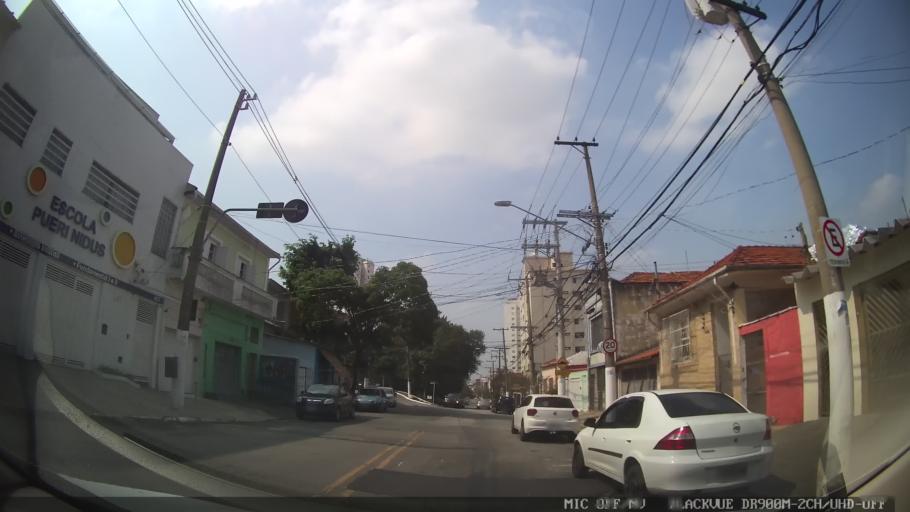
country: BR
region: Sao Paulo
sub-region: Sao Paulo
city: Sao Paulo
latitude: -23.5797
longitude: -46.6215
